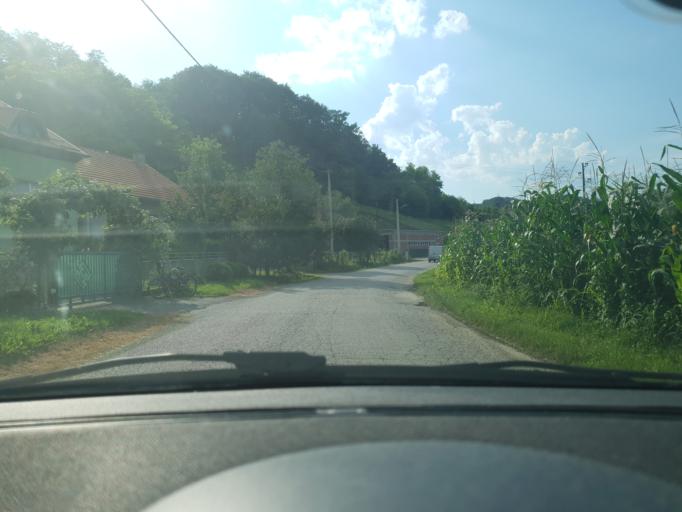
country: HR
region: Zagrebacka
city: Jakovlje
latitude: 46.0299
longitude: 15.8268
